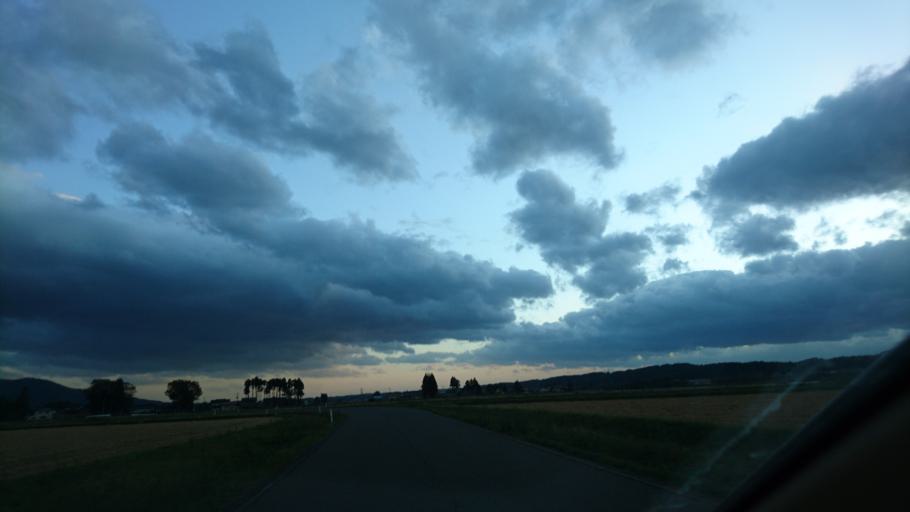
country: JP
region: Iwate
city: Mizusawa
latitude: 39.0764
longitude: 141.1413
